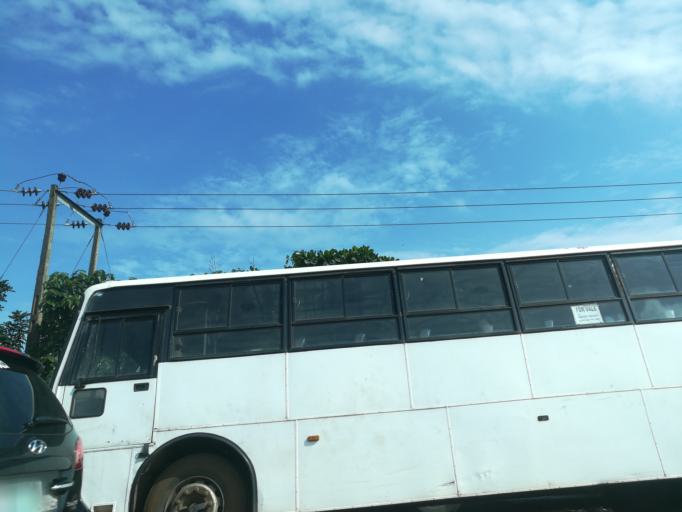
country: NG
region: Lagos
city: Ikorodu
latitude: 6.6294
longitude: 3.5122
